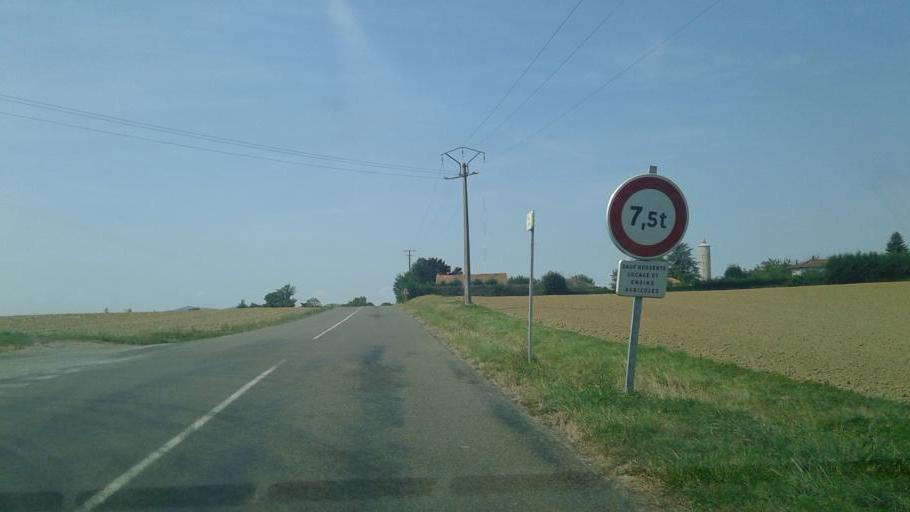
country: FR
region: Rhone-Alpes
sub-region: Departement de l'Ain
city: Tramoyes
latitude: 45.8747
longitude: 4.9713
